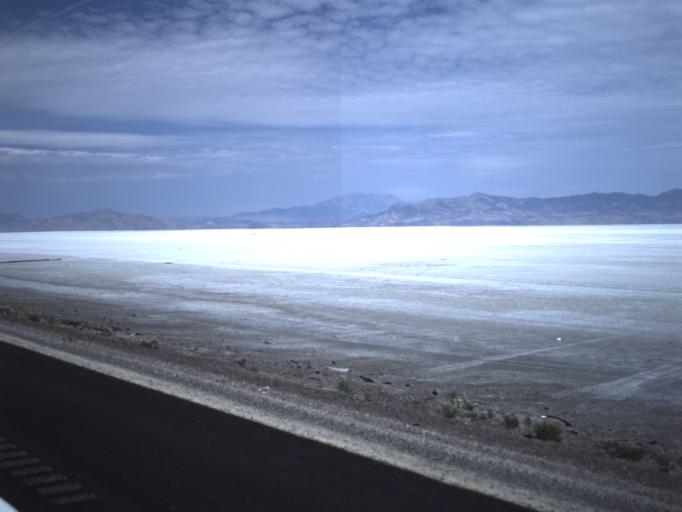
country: US
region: Utah
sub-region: Tooele County
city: Wendover
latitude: 40.7345
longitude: -113.6177
